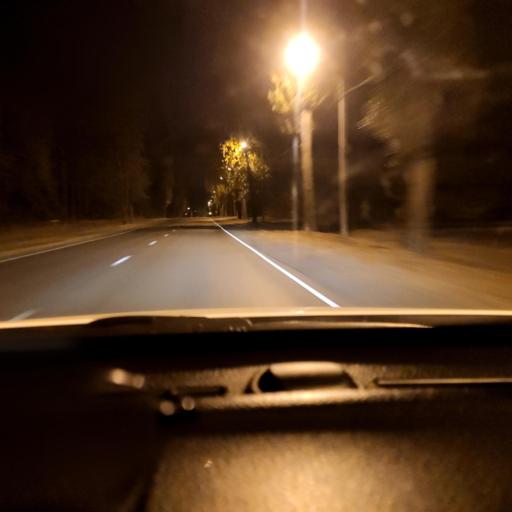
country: RU
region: Voronezj
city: Somovo
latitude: 51.6978
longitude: 39.3178
